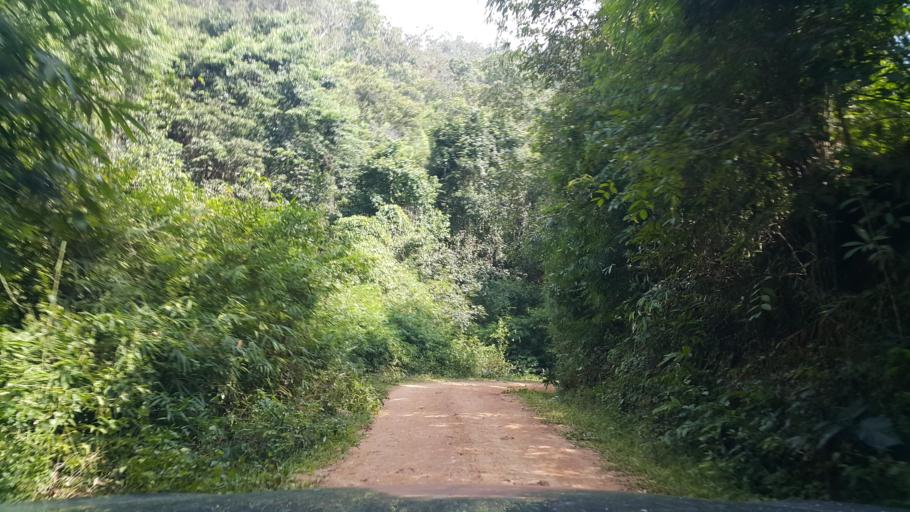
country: TH
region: Chiang Mai
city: Phrao
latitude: 19.0882
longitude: 99.2565
